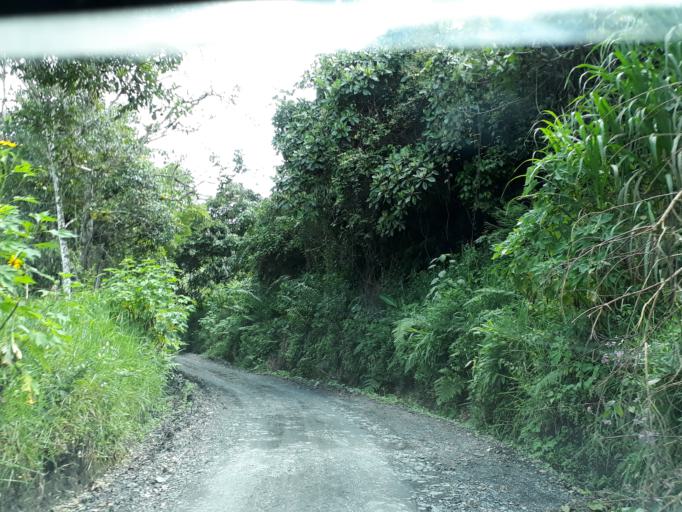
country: CO
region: Boyaca
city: Quipama
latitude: 5.4080
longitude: -74.1990
